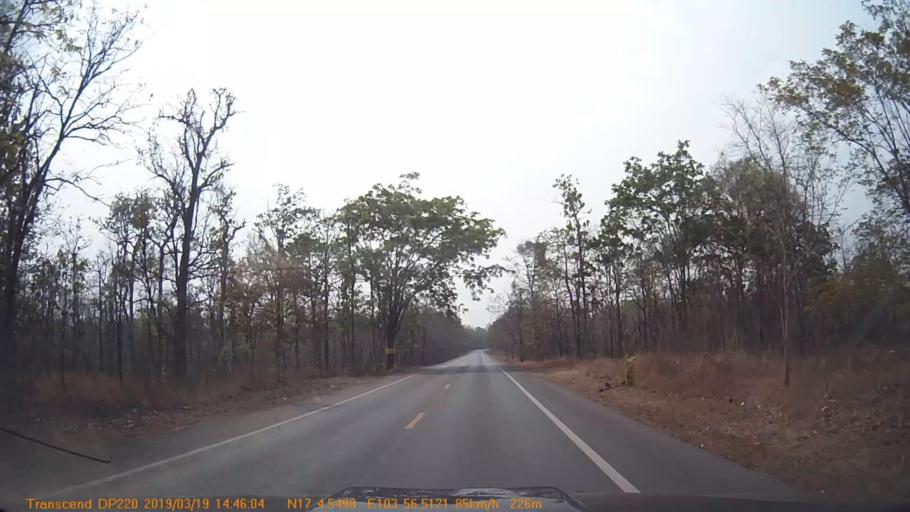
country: TH
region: Sakon Nakhon
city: Phu Phan
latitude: 17.0760
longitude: 103.9415
